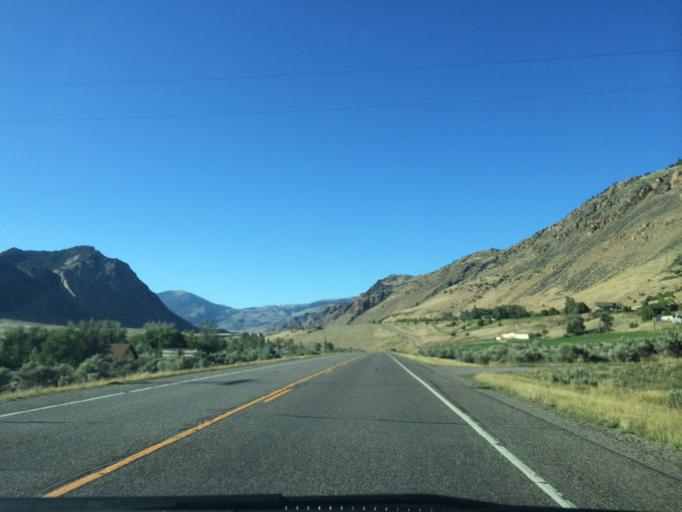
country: US
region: Montana
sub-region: Gallatin County
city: West Yellowstone
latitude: 45.0705
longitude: -110.7681
